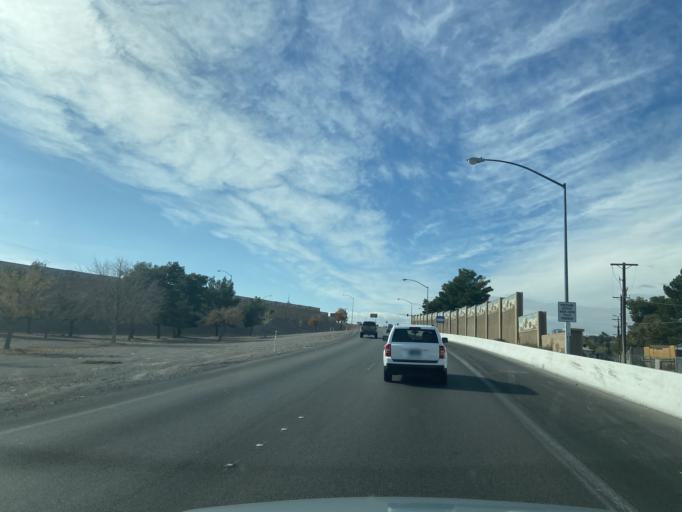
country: US
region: Nevada
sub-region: Clark County
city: Las Vegas
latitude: 36.1689
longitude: -115.1165
